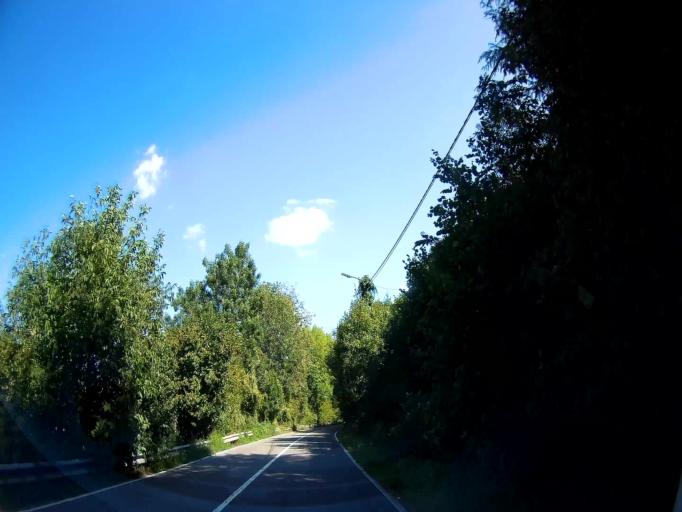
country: BE
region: Wallonia
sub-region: Province de Namur
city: Hastiere-Lavaux
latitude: 50.2144
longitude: 4.8316
